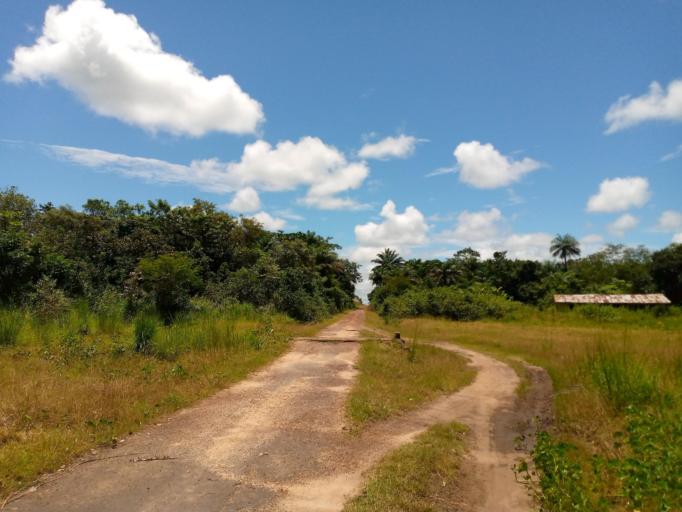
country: SL
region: Northern Province
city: Binkolo
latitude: 9.0786
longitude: -12.1440
